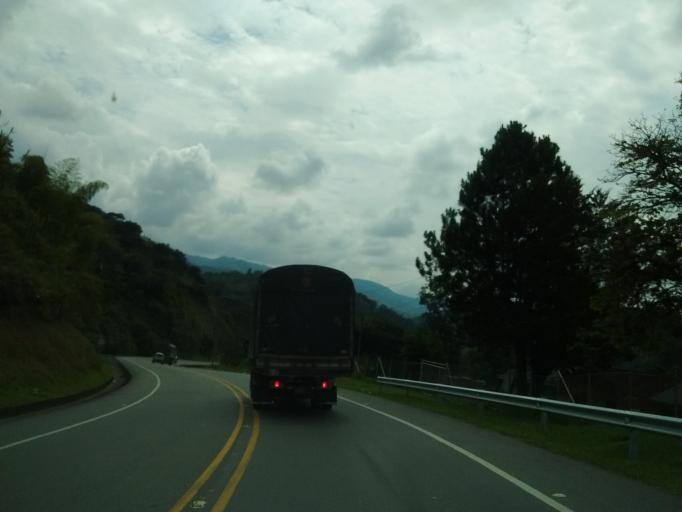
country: CO
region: Cauca
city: Morales
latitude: 2.7288
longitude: -76.5453
